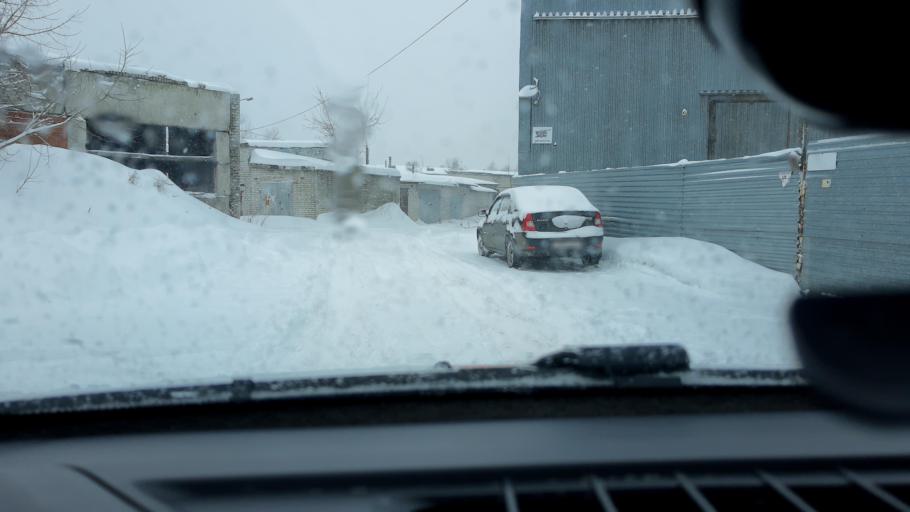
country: RU
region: Nizjnij Novgorod
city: Gorbatovka
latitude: 56.3562
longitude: 43.8439
